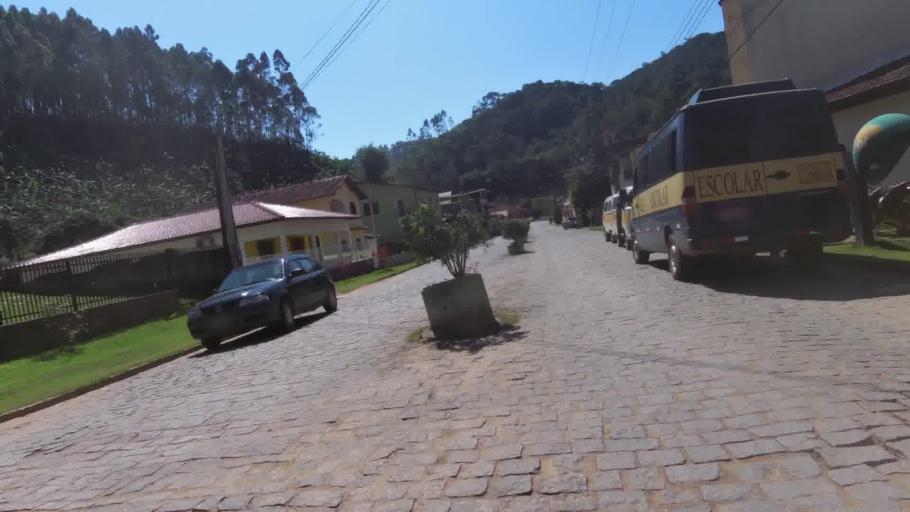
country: BR
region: Espirito Santo
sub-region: Alfredo Chaves
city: Alfredo Chaves
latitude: -20.5541
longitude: -40.8151
